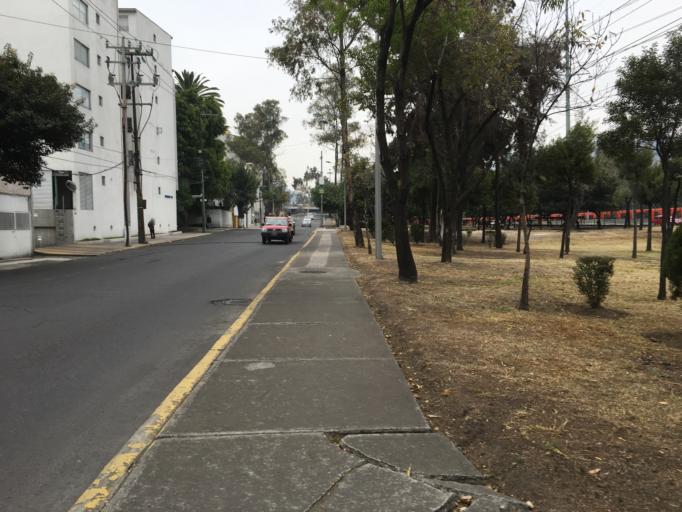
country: MX
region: Mexico
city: Colonia Lindavista
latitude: 19.4907
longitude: -99.1218
